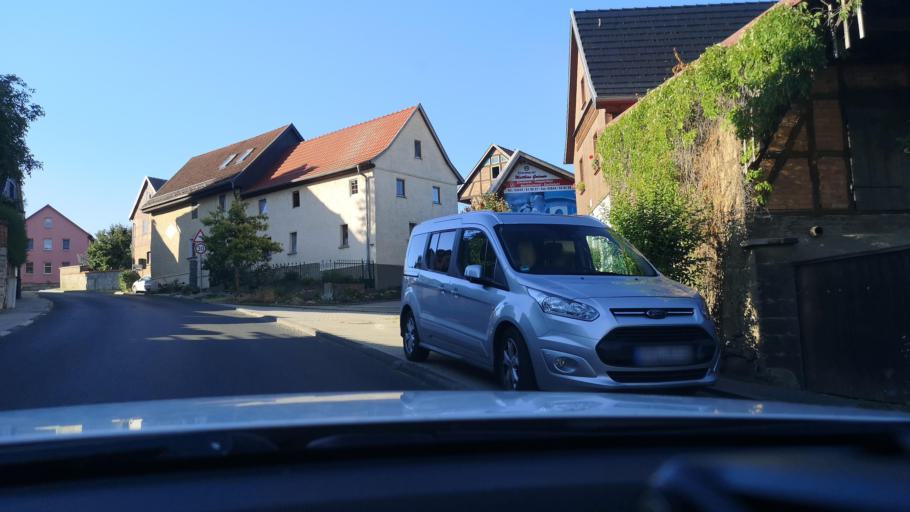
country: DE
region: Thuringia
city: Eberstedt
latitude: 51.0281
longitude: 11.5621
